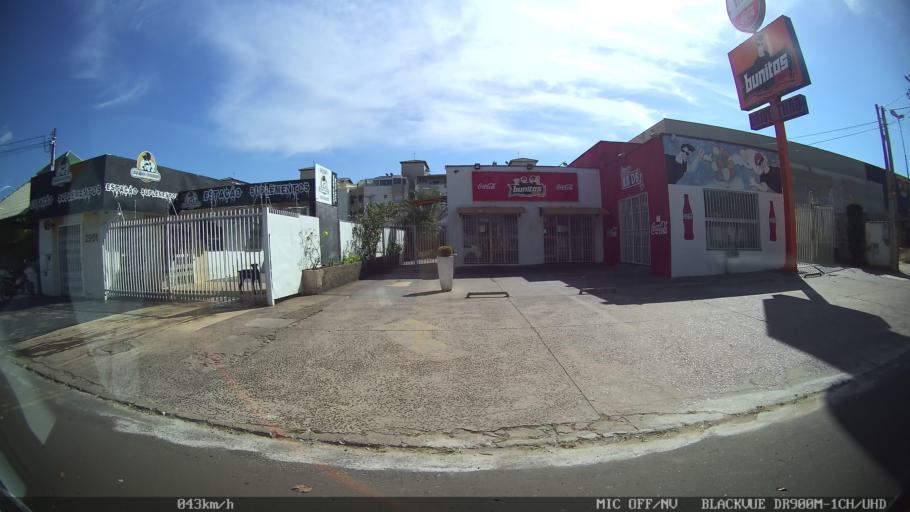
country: BR
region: Sao Paulo
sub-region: Franca
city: Franca
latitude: -20.5248
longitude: -47.4110
